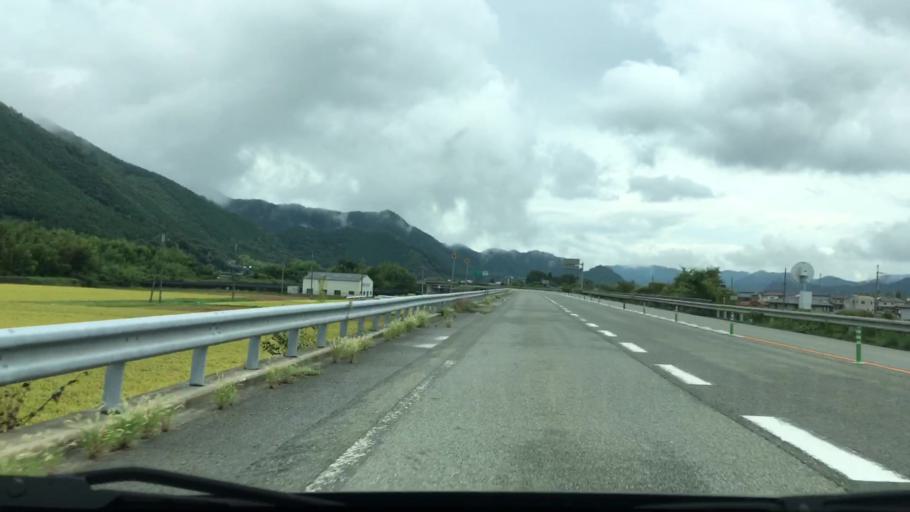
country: JP
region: Hyogo
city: Yamazakicho-nakabirose
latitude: 35.0530
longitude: 134.7639
